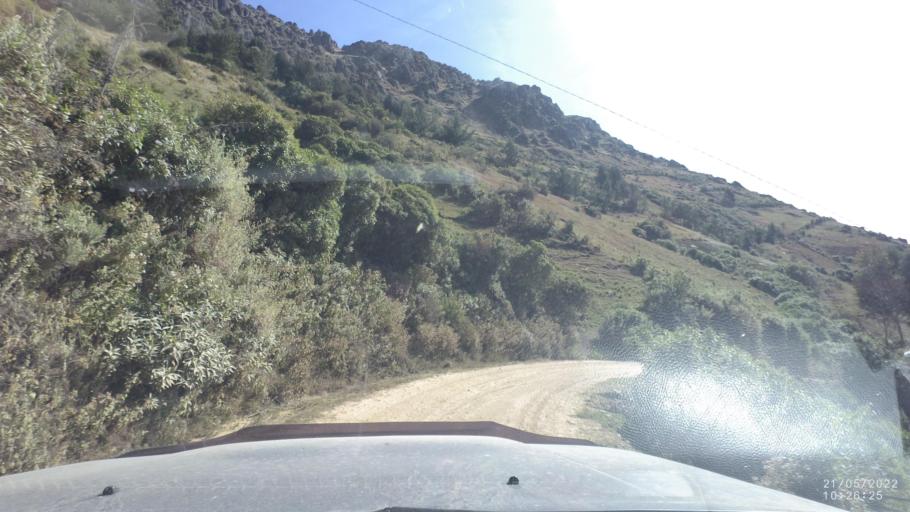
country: BO
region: Cochabamba
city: Colomi
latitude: -17.3248
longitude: -65.9472
